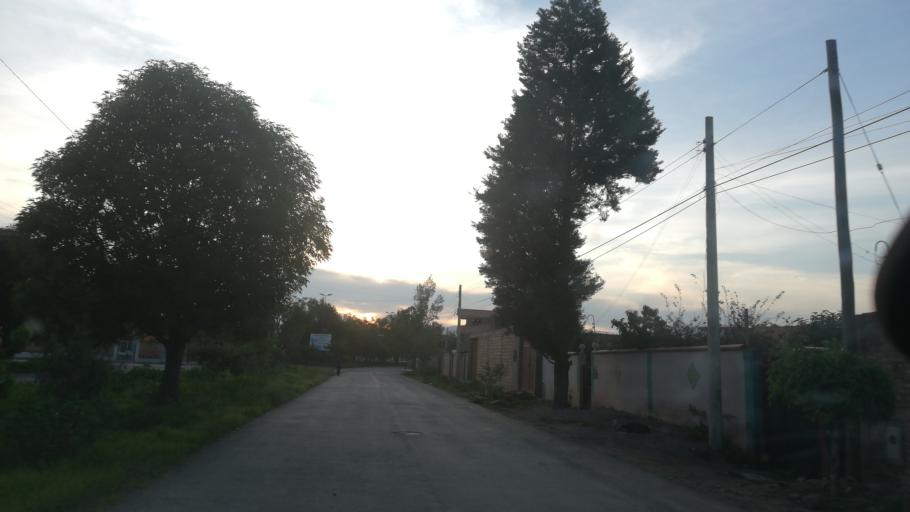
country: BO
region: Cochabamba
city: Cochabamba
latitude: -17.3828
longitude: -66.2061
